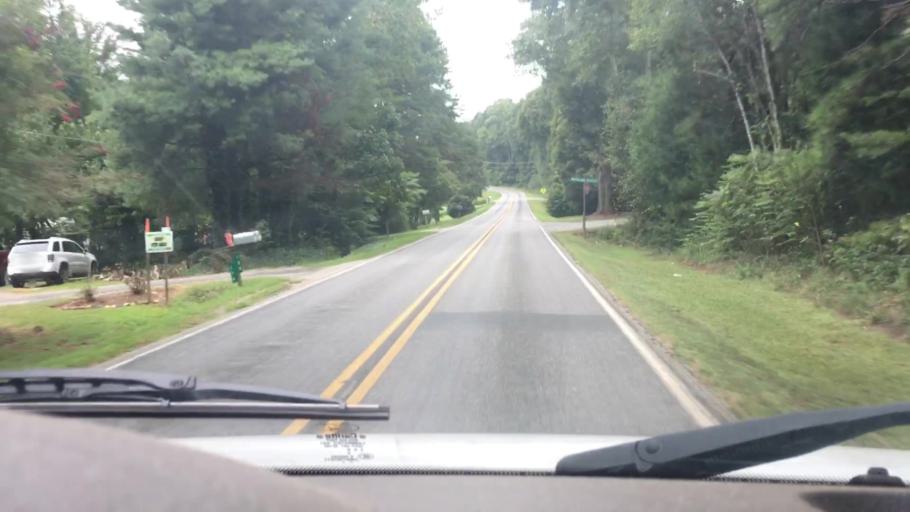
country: US
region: North Carolina
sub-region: Gaston County
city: Davidson
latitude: 35.5174
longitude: -80.8339
